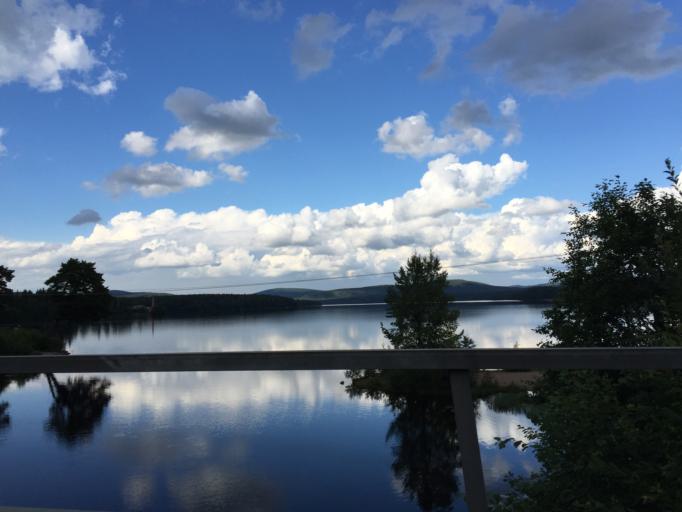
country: SE
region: Gaevleborg
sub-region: Ljusdals Kommun
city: Jaervsoe
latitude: 61.6658
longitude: 16.3128
